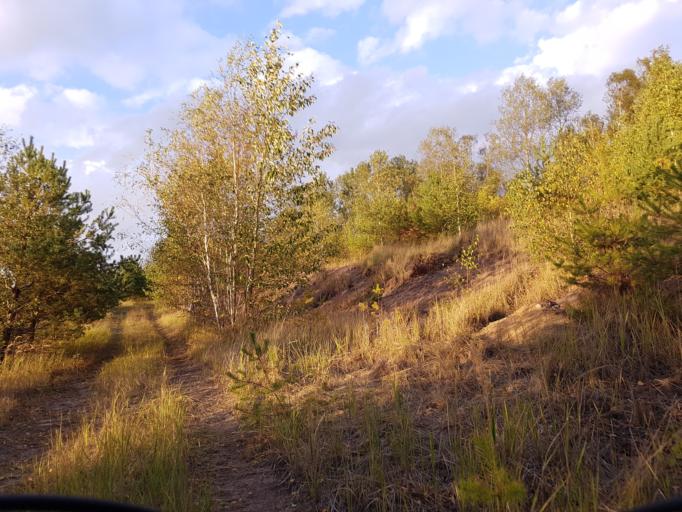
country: DE
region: Brandenburg
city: Trobitz
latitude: 51.5851
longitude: 13.4406
